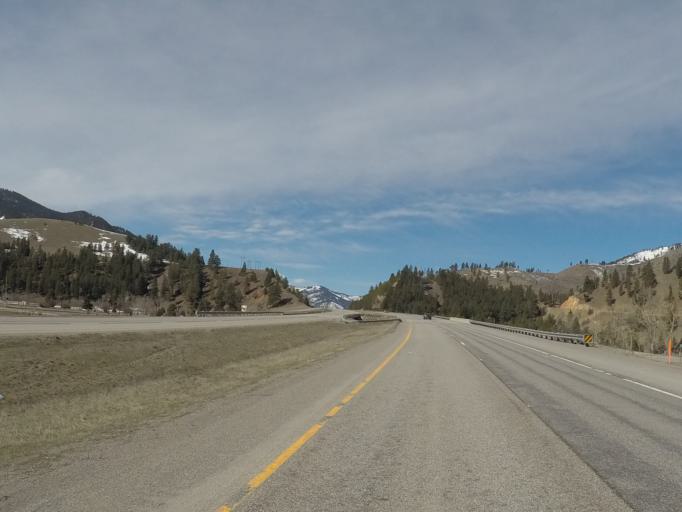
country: US
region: Montana
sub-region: Missoula County
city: Clinton
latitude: 46.7254
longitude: -113.5741
